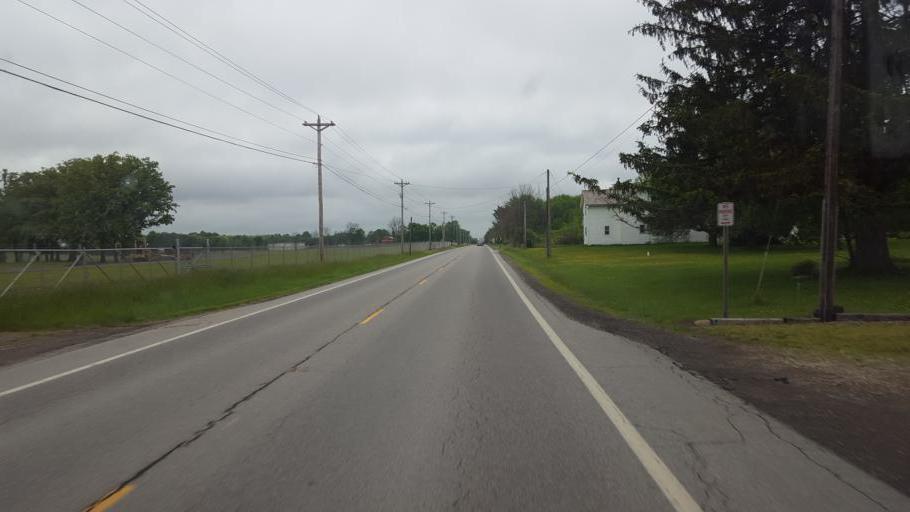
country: US
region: Ohio
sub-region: Wayne County
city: West Salem
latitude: 40.9817
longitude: -82.0961
